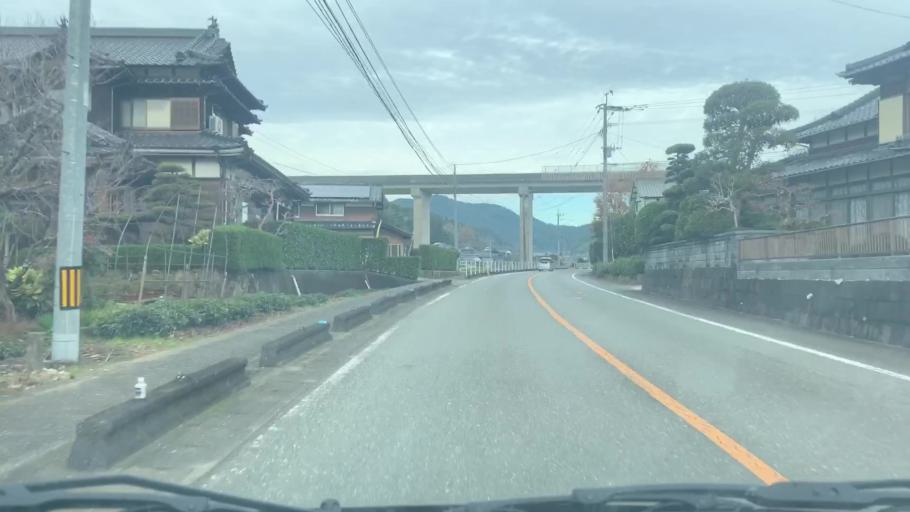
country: JP
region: Saga Prefecture
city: Ureshinomachi-shimojuku
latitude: 33.1421
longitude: 129.9769
